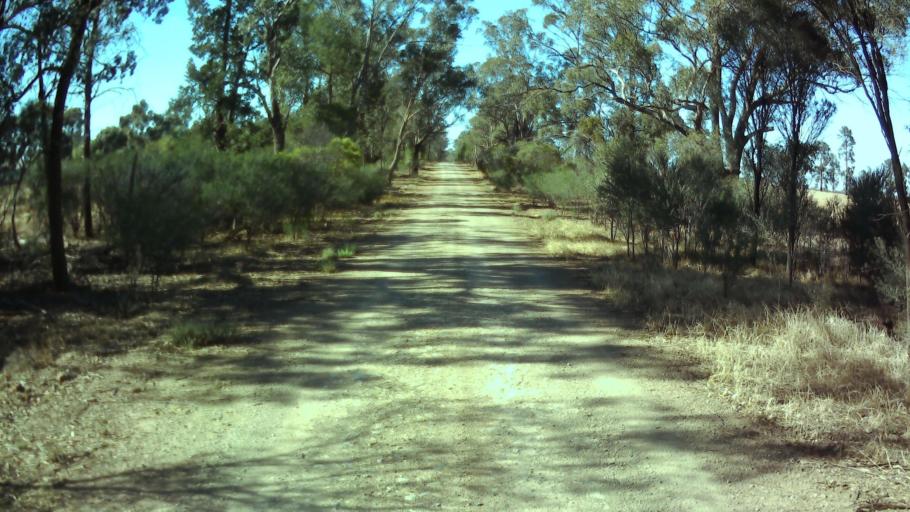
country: AU
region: New South Wales
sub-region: Weddin
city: Grenfell
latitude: -33.9243
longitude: 147.8741
